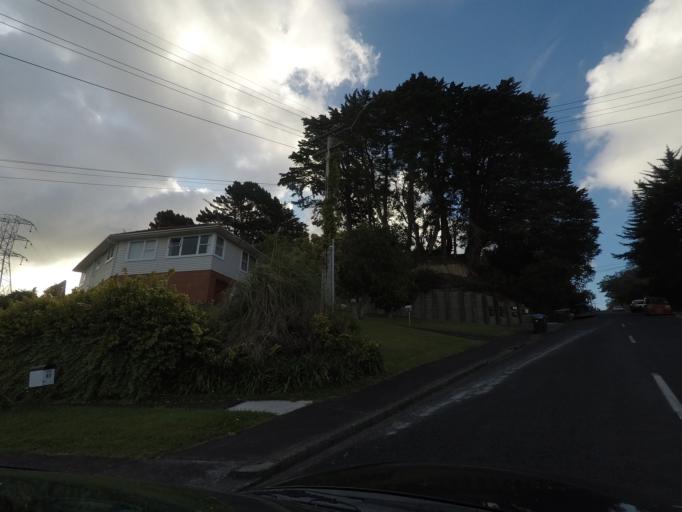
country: NZ
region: Auckland
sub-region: Auckland
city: Mangere
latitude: -36.9250
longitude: 174.7586
